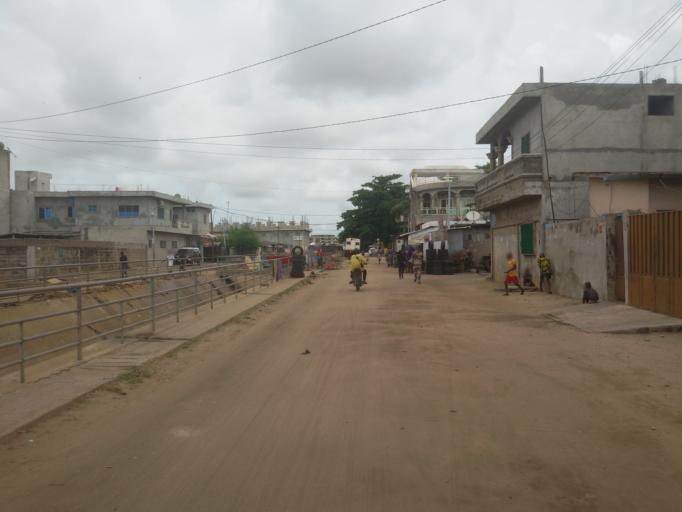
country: BJ
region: Littoral
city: Cotonou
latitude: 6.3799
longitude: 2.4404
